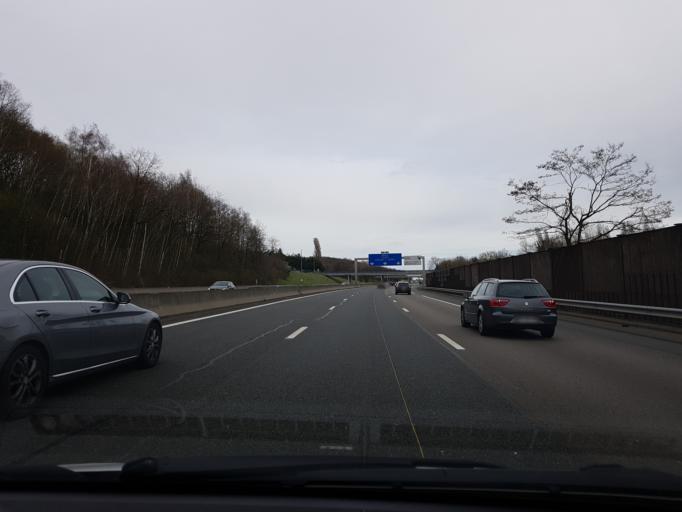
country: FR
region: Bourgogne
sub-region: Departement de Saone-et-Loire
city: Sance
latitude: 46.3653
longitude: 4.8330
